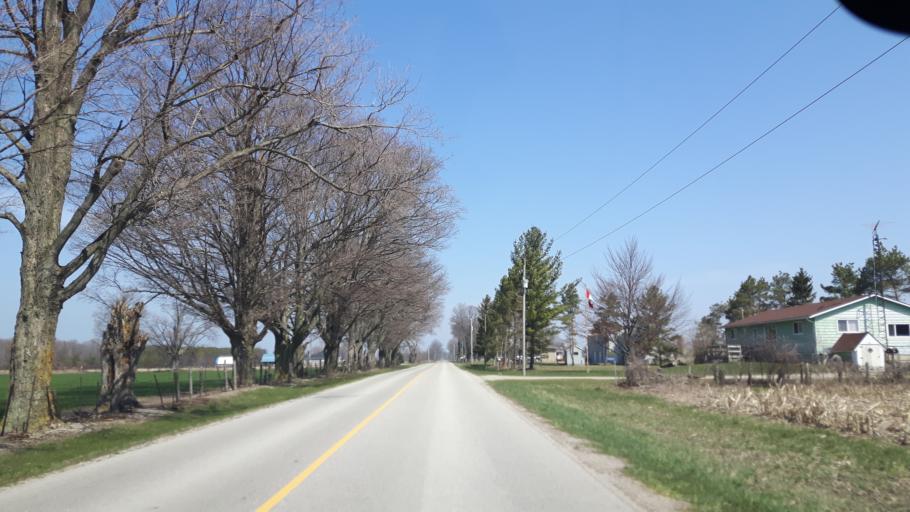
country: CA
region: Ontario
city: Goderich
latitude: 43.6708
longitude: -81.6846
